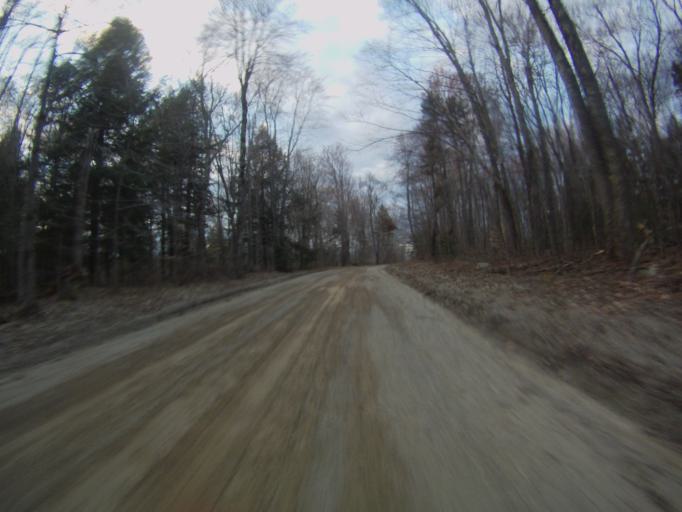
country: US
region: Vermont
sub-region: Rutland County
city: Brandon
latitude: 43.9381
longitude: -73.0216
